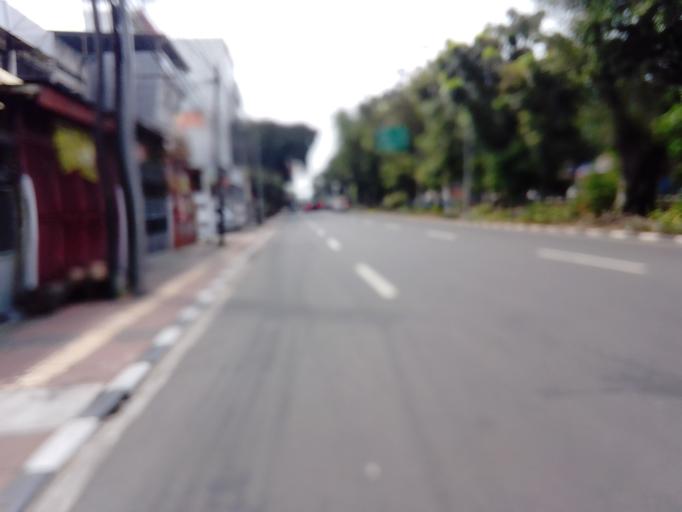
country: ID
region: Jakarta Raya
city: Jakarta
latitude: -6.1621
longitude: 106.8105
